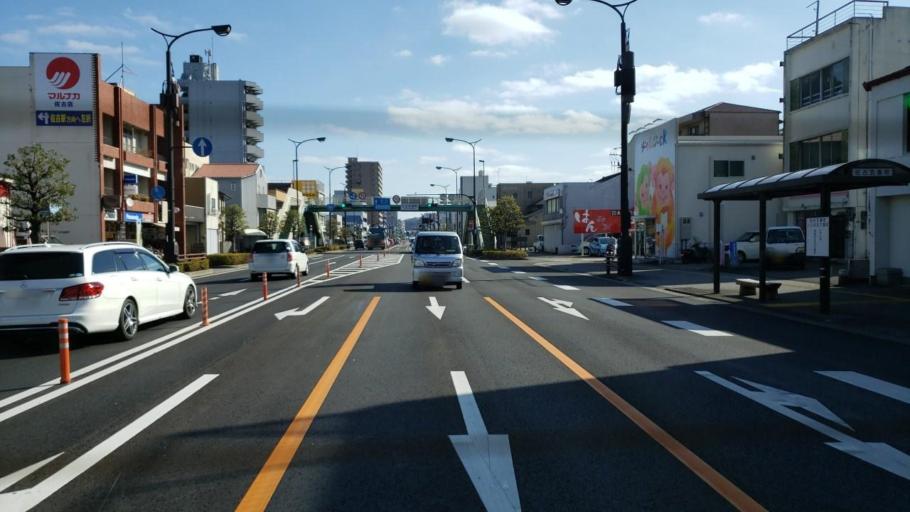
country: JP
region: Tokushima
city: Tokushima-shi
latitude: 34.0788
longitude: 134.5300
